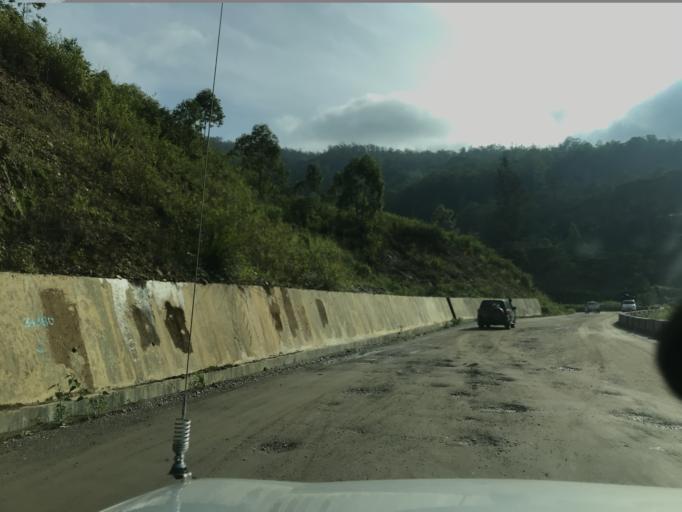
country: TL
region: Aileu
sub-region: Aileu Villa
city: Aileu
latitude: -8.6624
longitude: 125.5476
